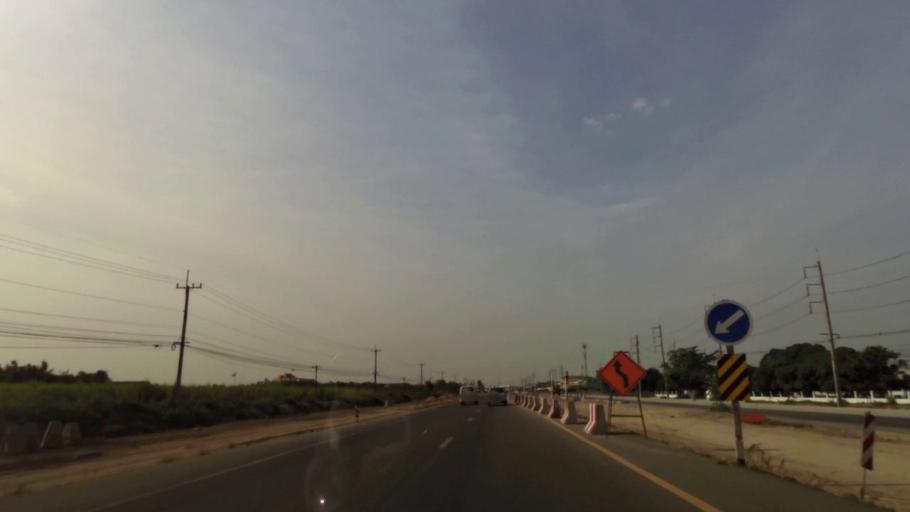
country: TH
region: Chon Buri
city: Ban Bueng
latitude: 13.2830
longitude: 101.1798
